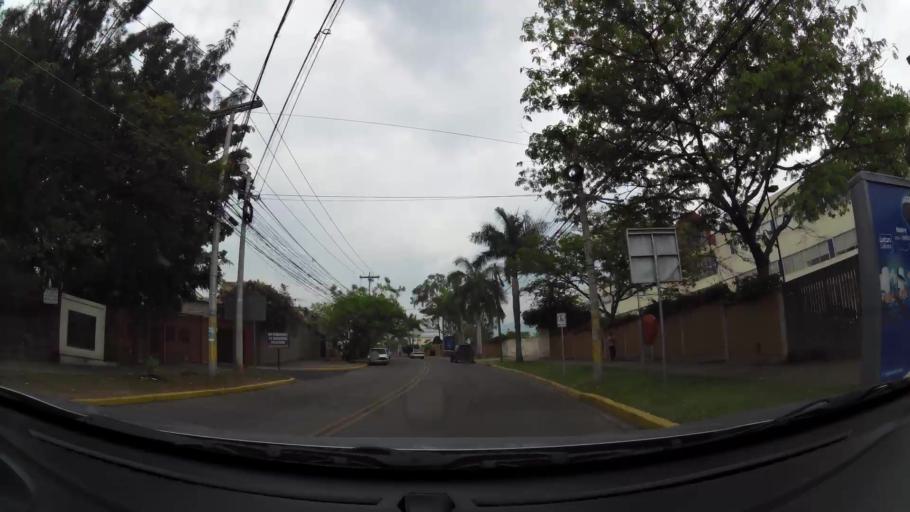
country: HN
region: Francisco Morazan
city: Tegucigalpa
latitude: 14.0793
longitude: -87.1832
